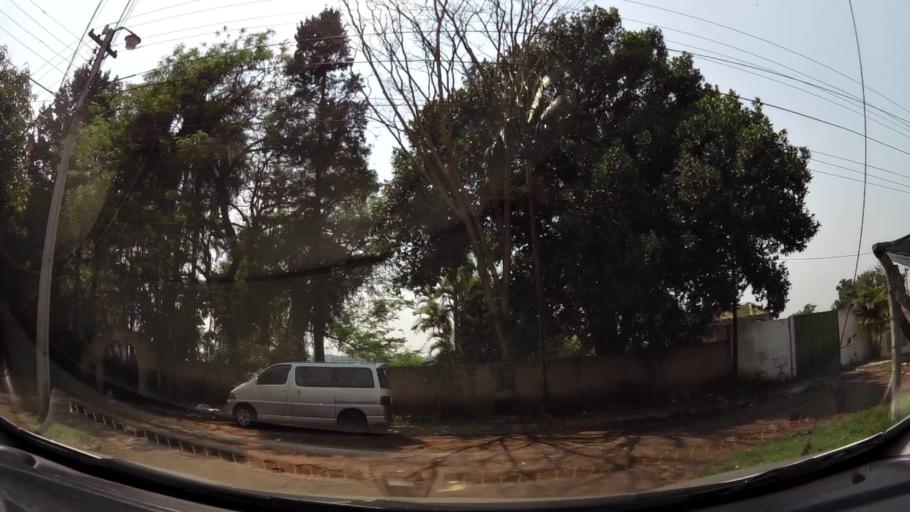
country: PY
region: Alto Parana
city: Ciudad del Este
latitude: -25.5153
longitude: -54.6077
